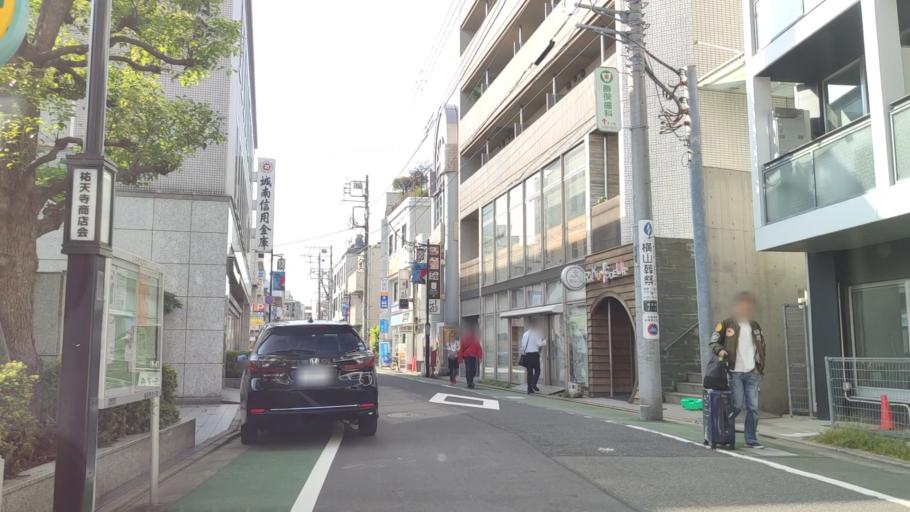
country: JP
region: Tokyo
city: Tokyo
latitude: 35.6375
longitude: 139.6913
